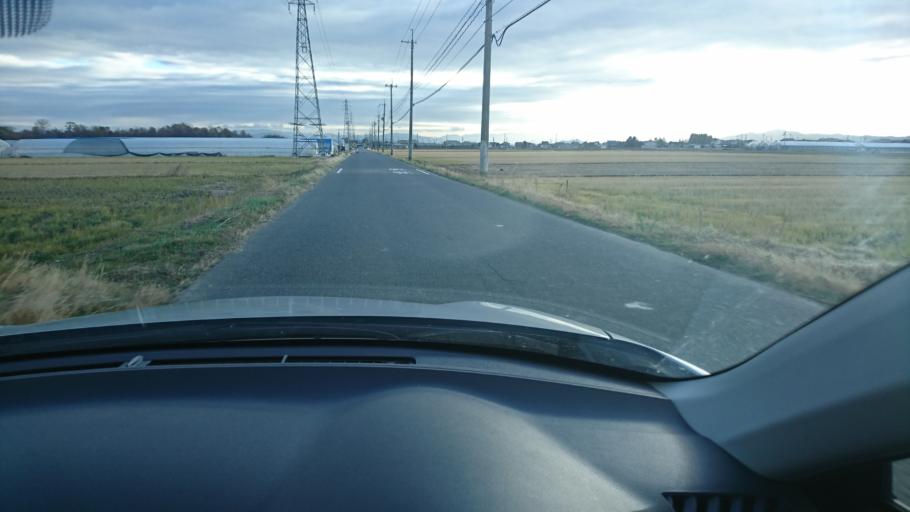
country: JP
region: Shiga Prefecture
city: Moriyama
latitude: 35.1288
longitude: 135.9867
